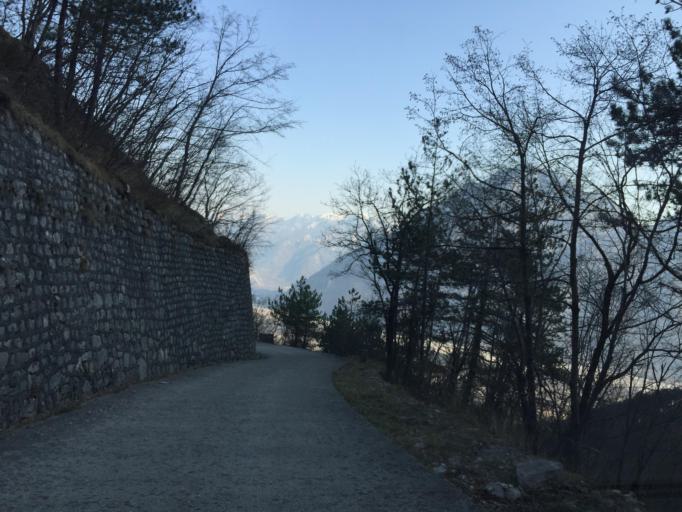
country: IT
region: Friuli Venezia Giulia
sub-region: Provincia di Udine
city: Amaro
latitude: 46.3853
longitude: 13.0817
